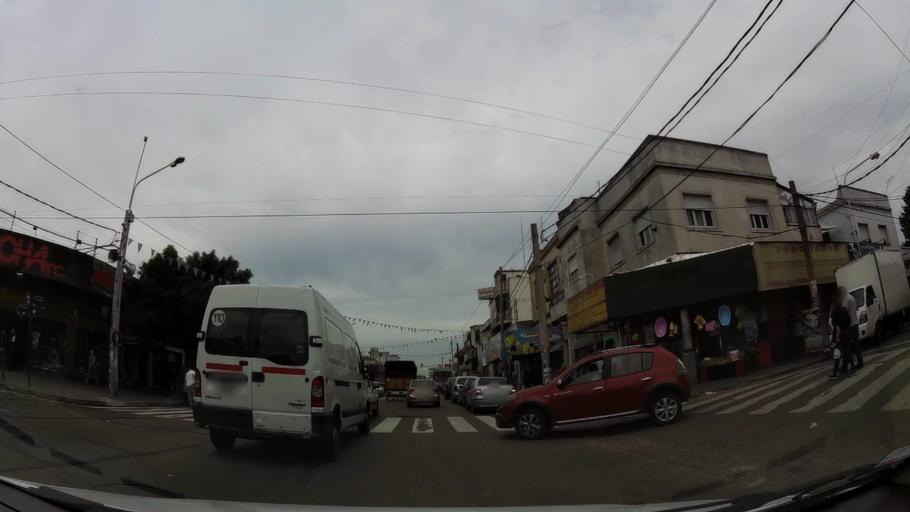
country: AR
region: Buenos Aires F.D.
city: Villa Lugano
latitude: -34.6794
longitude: -58.5102
